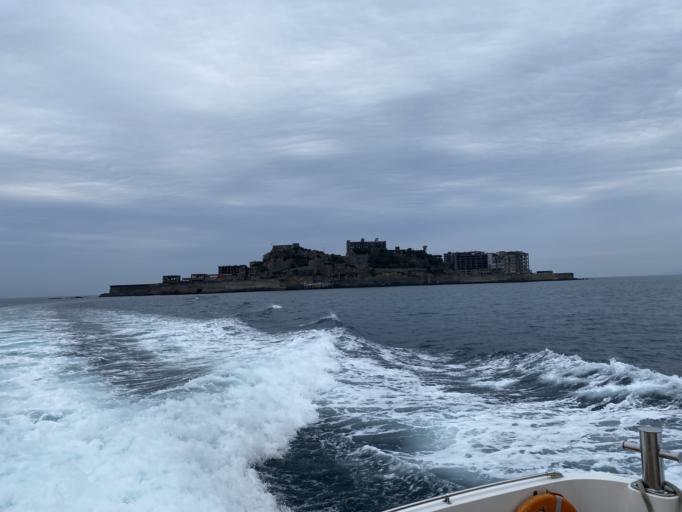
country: JP
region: Nagasaki
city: Nagasaki-shi
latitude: 32.6240
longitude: 129.7422
